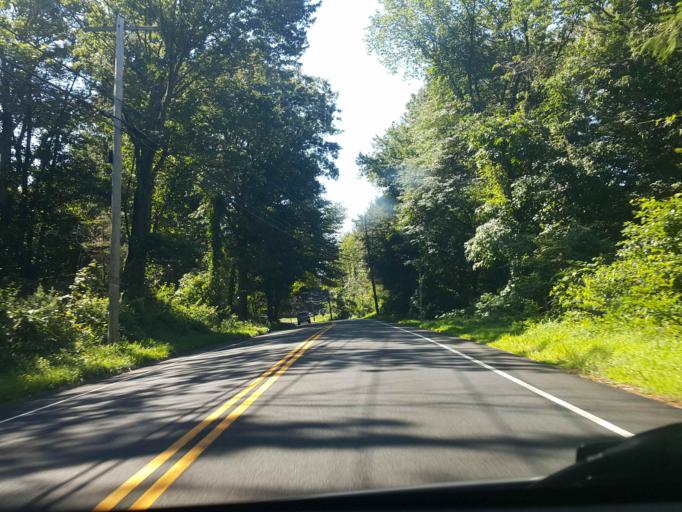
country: US
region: Connecticut
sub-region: New Haven County
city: Guilford
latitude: 41.3045
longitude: -72.6888
